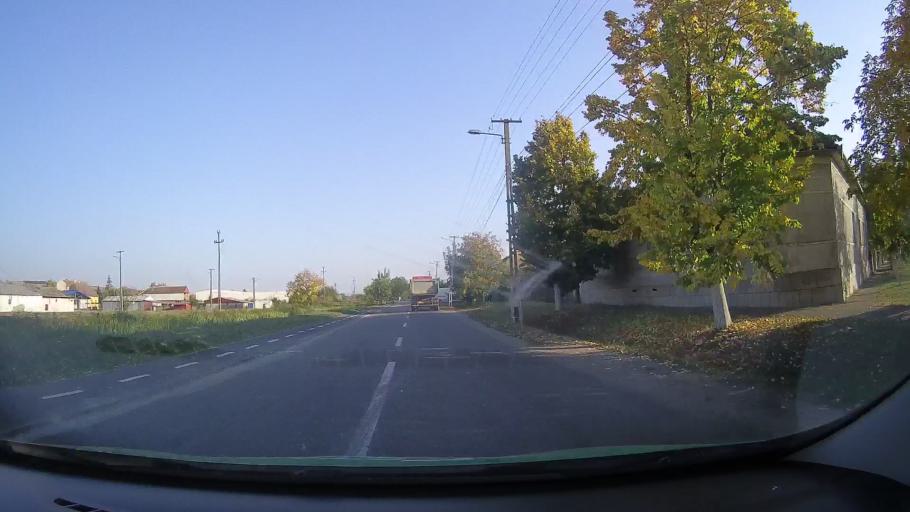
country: RO
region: Arad
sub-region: Comuna Pancota
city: Pancota
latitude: 46.3223
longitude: 21.6904
